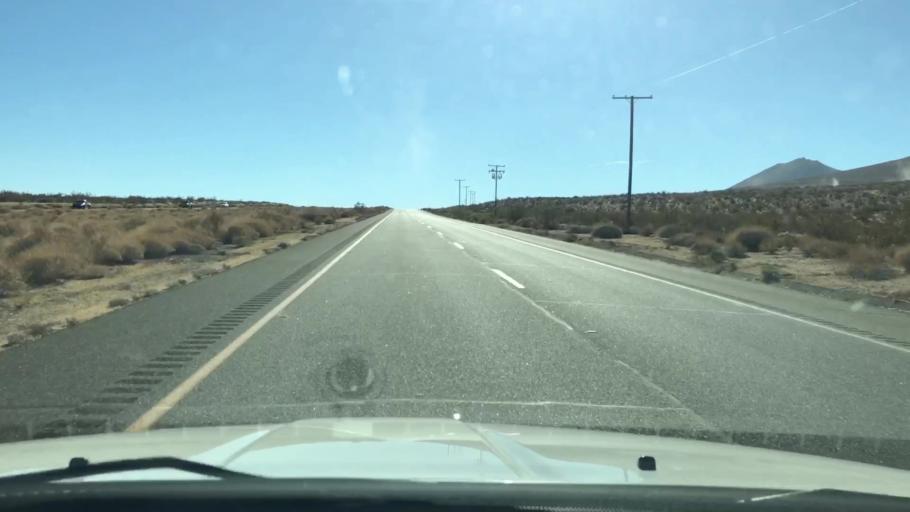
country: US
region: California
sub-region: Kern County
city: Inyokern
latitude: 35.6779
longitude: -117.8682
